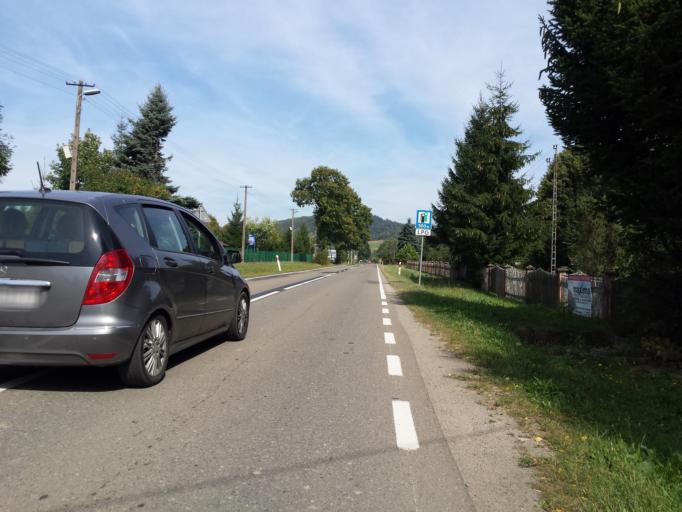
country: PL
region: Subcarpathian Voivodeship
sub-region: Powiat leski
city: Baligrod
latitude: 49.3457
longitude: 22.2898
